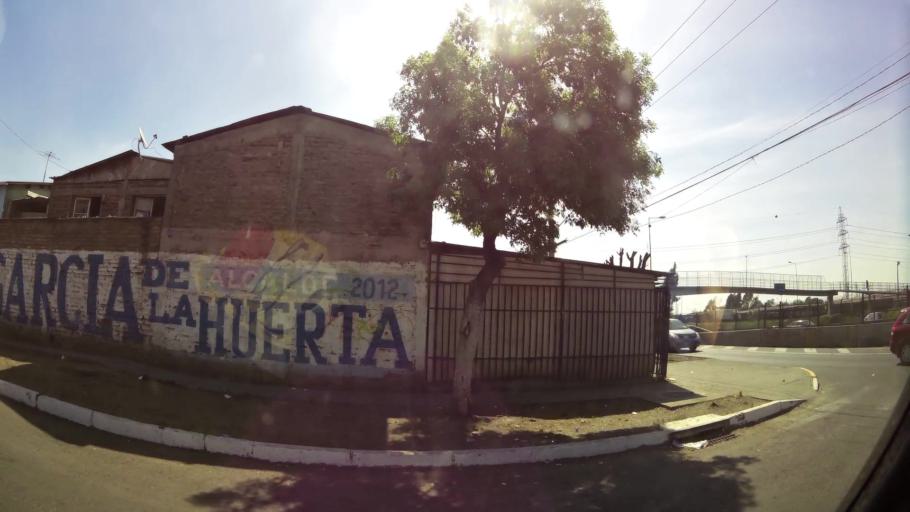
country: CL
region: Santiago Metropolitan
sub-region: Provincia de Maipo
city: San Bernardo
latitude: -33.5253
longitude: -70.6966
